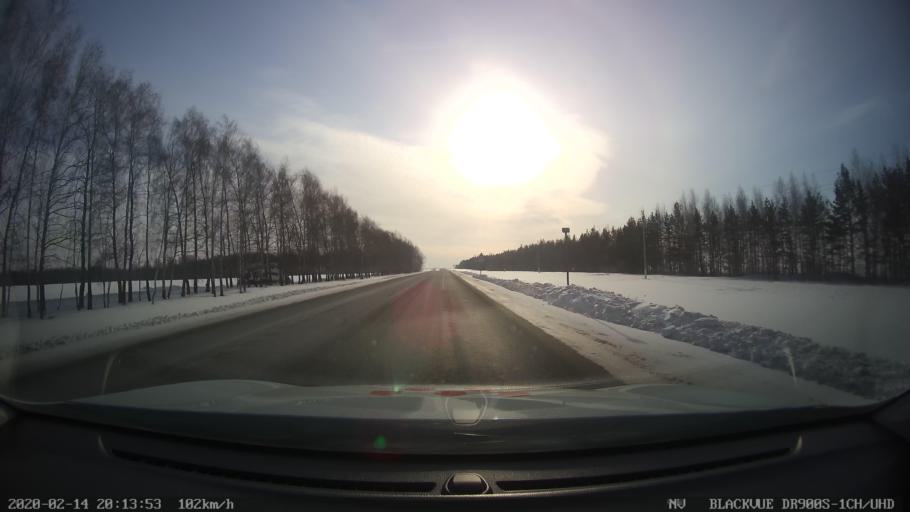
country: RU
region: Tatarstan
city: Verkhniy Uslon
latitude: 55.6528
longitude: 48.8672
